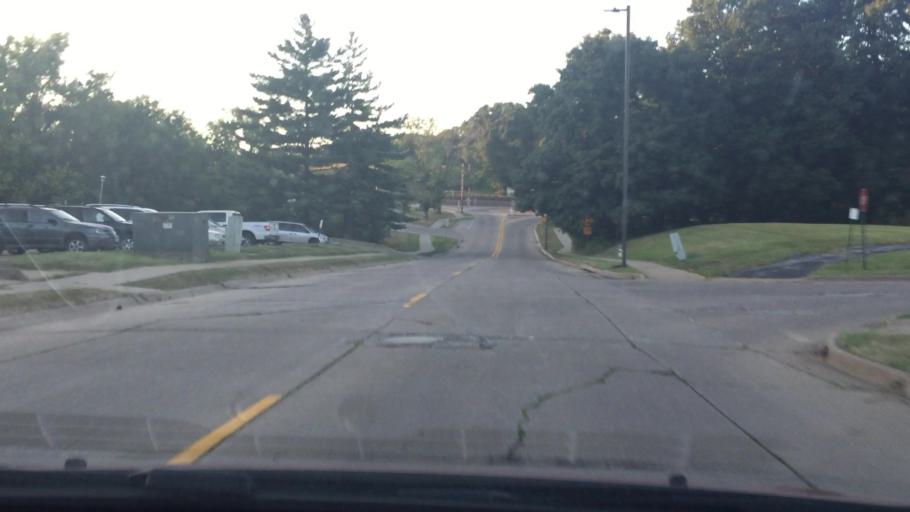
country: US
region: Iowa
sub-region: Muscatine County
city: Muscatine
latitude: 41.4341
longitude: -91.0649
